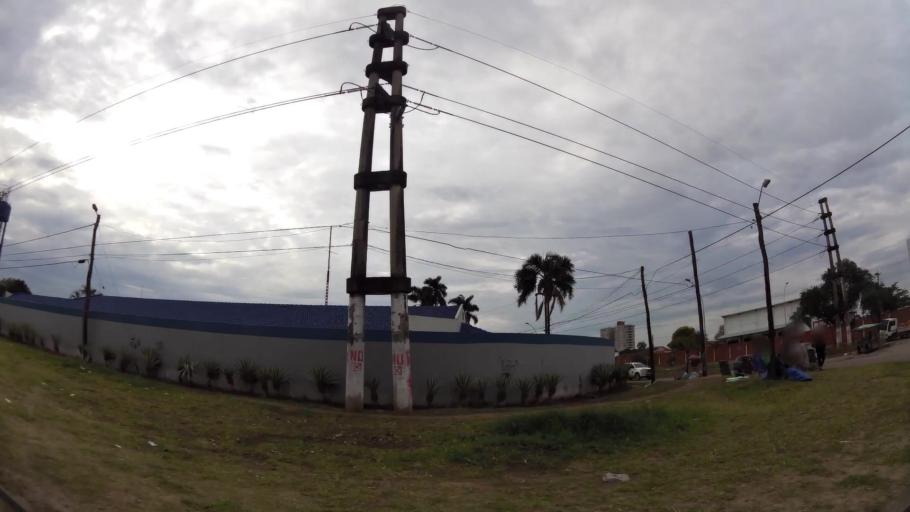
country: BO
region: Santa Cruz
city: Santa Cruz de la Sierra
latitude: -17.7424
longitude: -63.1652
